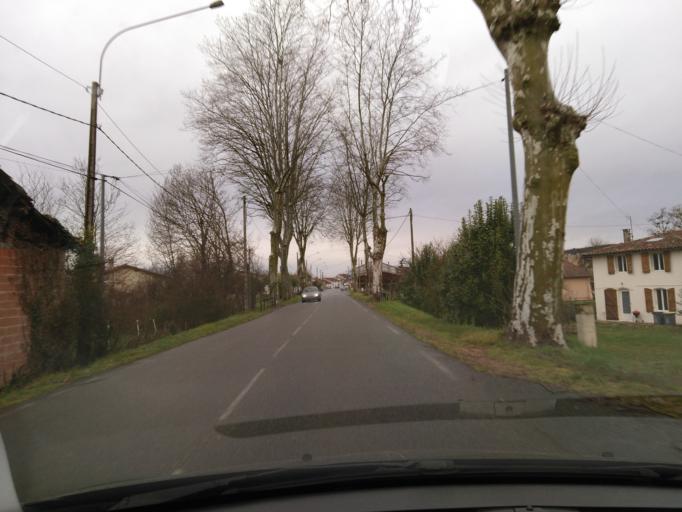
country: FR
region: Midi-Pyrenees
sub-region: Departement de la Haute-Garonne
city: Montesquieu-Volvestre
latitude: 43.2004
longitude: 1.2298
